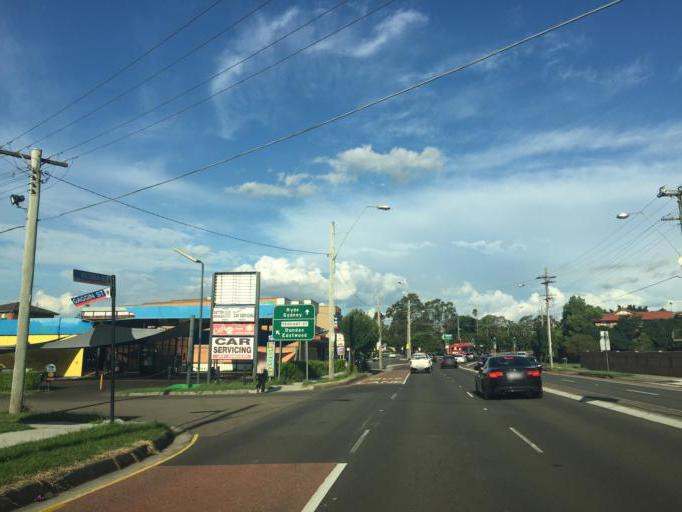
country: AU
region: New South Wales
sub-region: Parramatta
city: Paramatta
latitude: -33.8085
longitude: 151.0172
